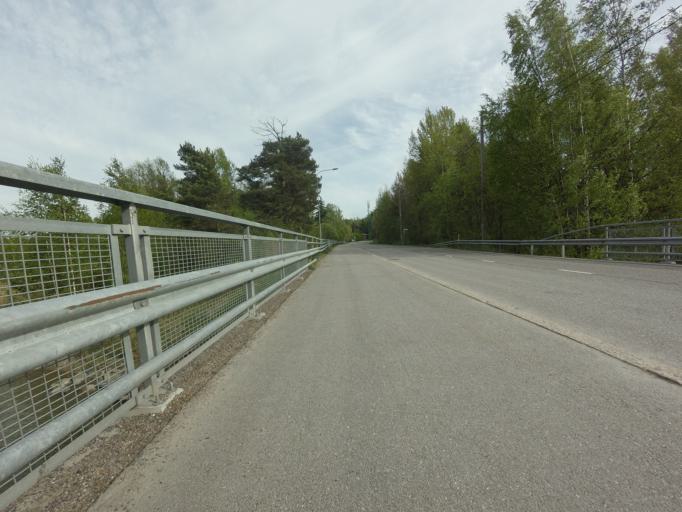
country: FI
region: Uusimaa
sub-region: Helsinki
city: Koukkuniemi
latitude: 60.1223
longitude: 24.7154
